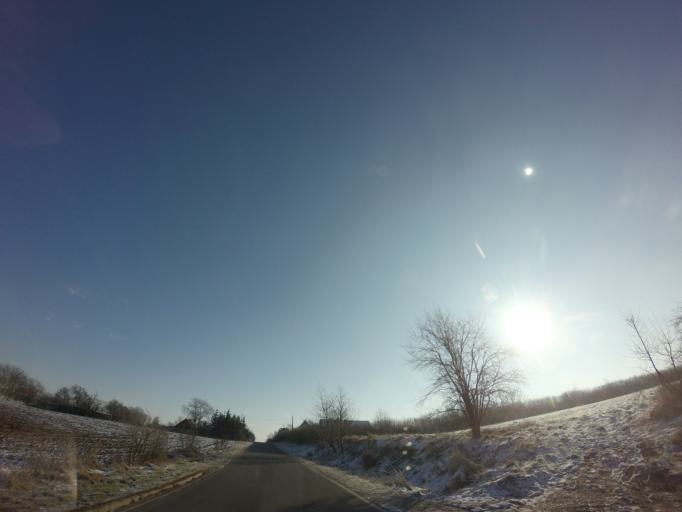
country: PL
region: West Pomeranian Voivodeship
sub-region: Powiat choszczenski
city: Pelczyce
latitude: 53.0354
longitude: 15.3268
